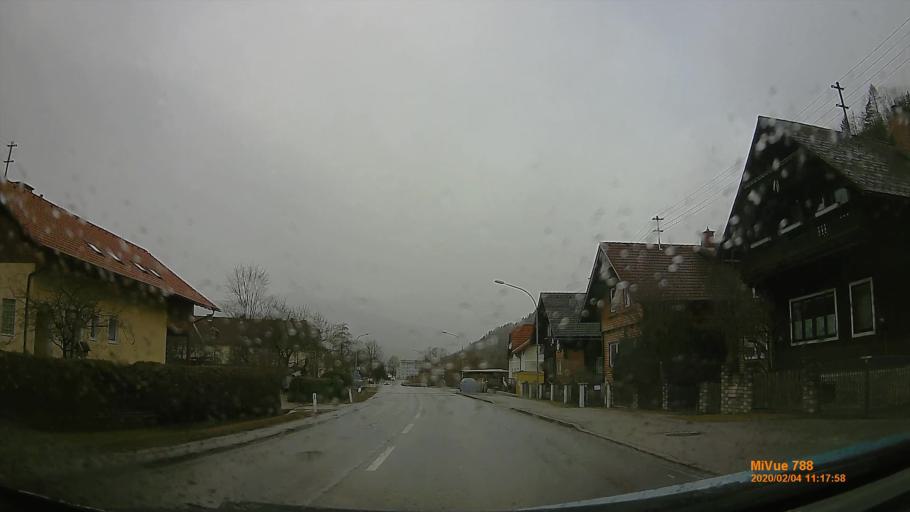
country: AT
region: Styria
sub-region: Politischer Bezirk Bruck-Muerzzuschlag
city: Muerzzuschlag
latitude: 47.6057
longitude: 15.6981
